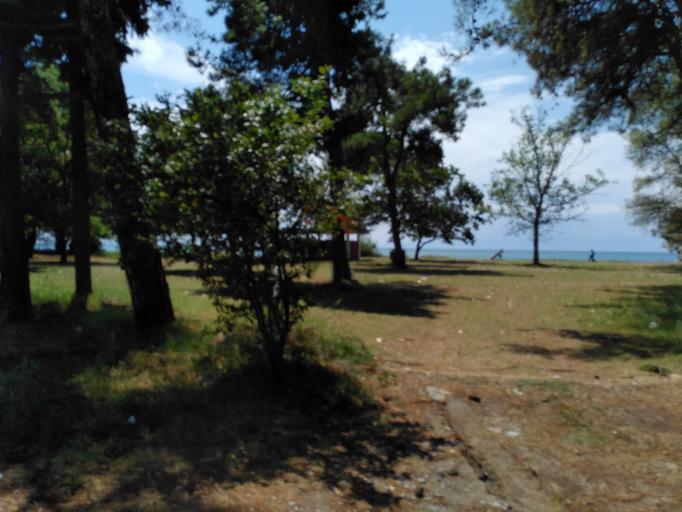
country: GR
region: Central Macedonia
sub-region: Nomos Thessalonikis
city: Nea Michaniona
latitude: 40.4294
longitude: 22.8779
